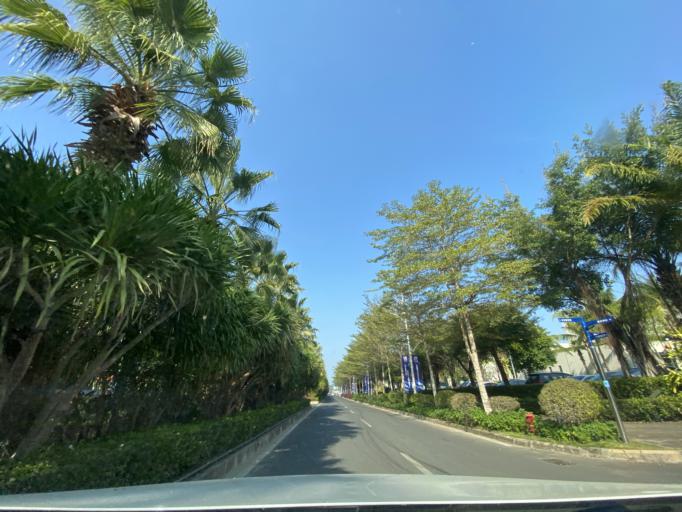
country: CN
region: Hainan
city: Yingzhou
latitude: 18.4114
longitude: 109.8536
